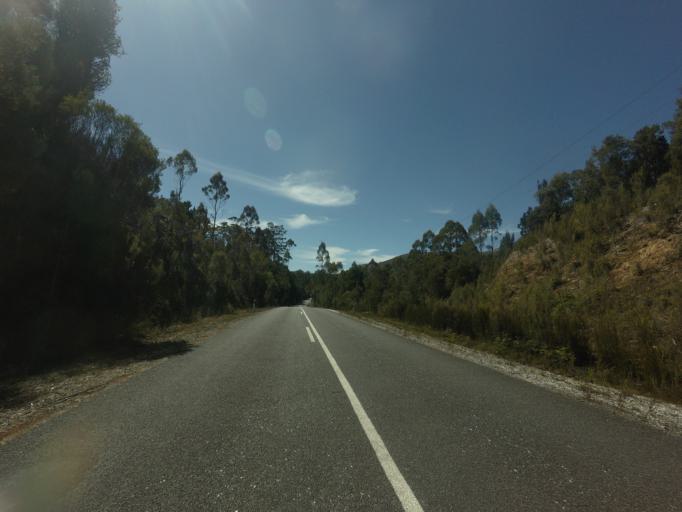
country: AU
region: Tasmania
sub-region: West Coast
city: Queenstown
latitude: -42.7705
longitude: 146.0434
